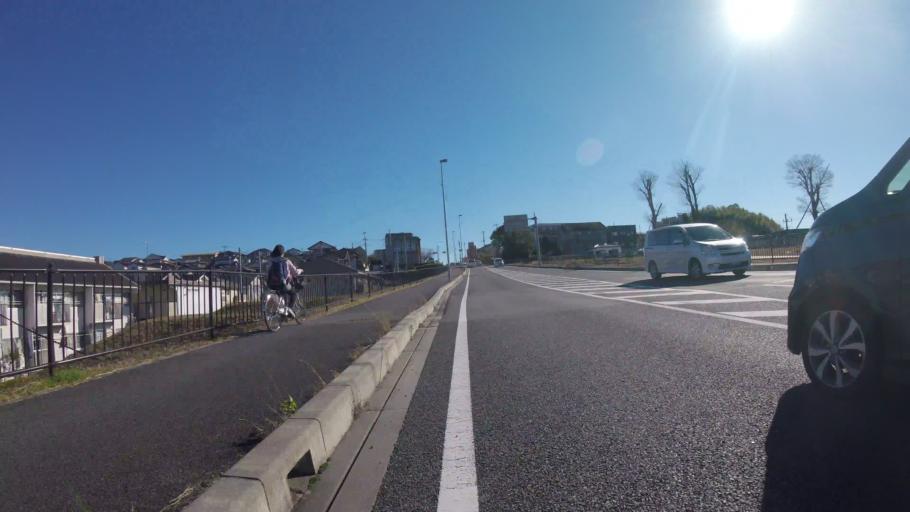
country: JP
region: Shizuoka
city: Mishima
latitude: 35.1295
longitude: 138.9257
